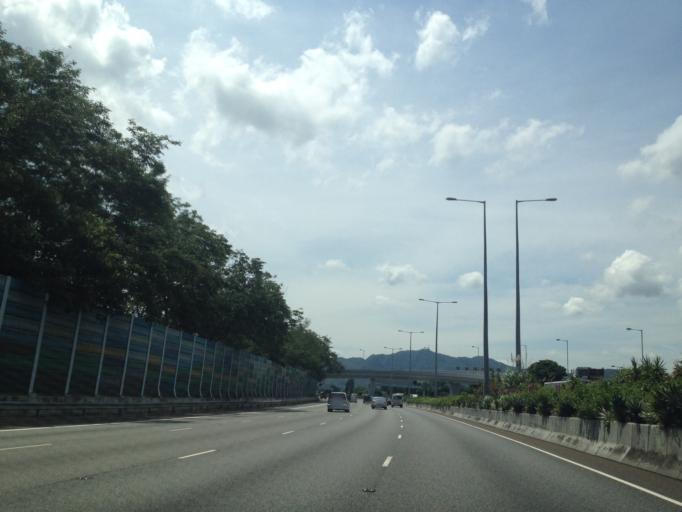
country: HK
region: Tai Po
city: Tai Po
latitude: 22.4349
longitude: 114.1999
